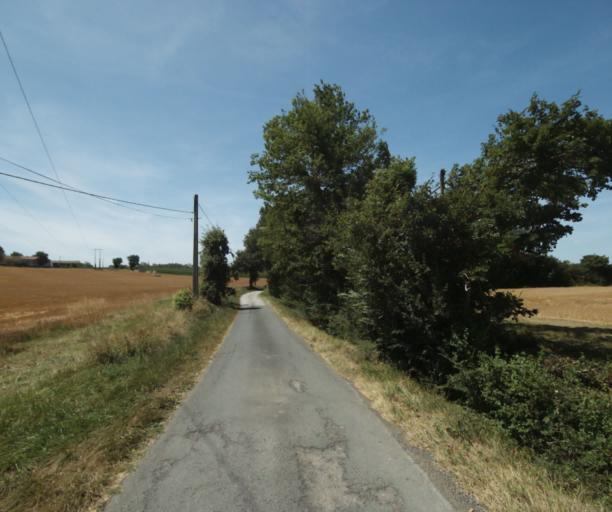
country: FR
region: Midi-Pyrenees
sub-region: Departement du Tarn
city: Soreze
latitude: 43.4909
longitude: 2.0434
